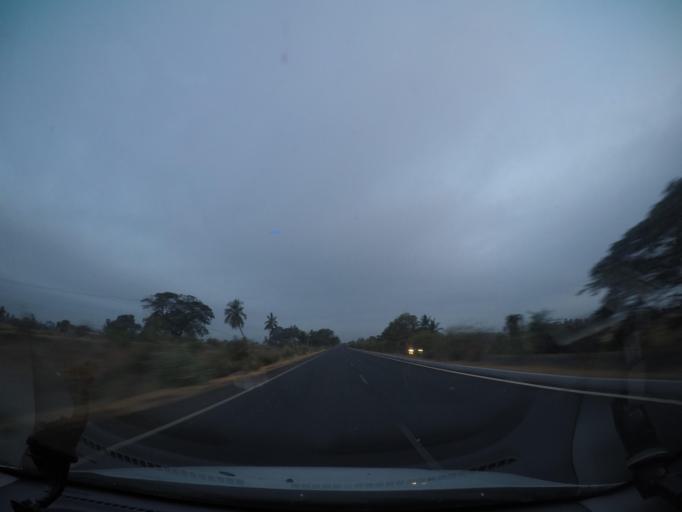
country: IN
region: Andhra Pradesh
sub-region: West Godavari
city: Tadepallegudem
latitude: 16.8098
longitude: 81.3551
